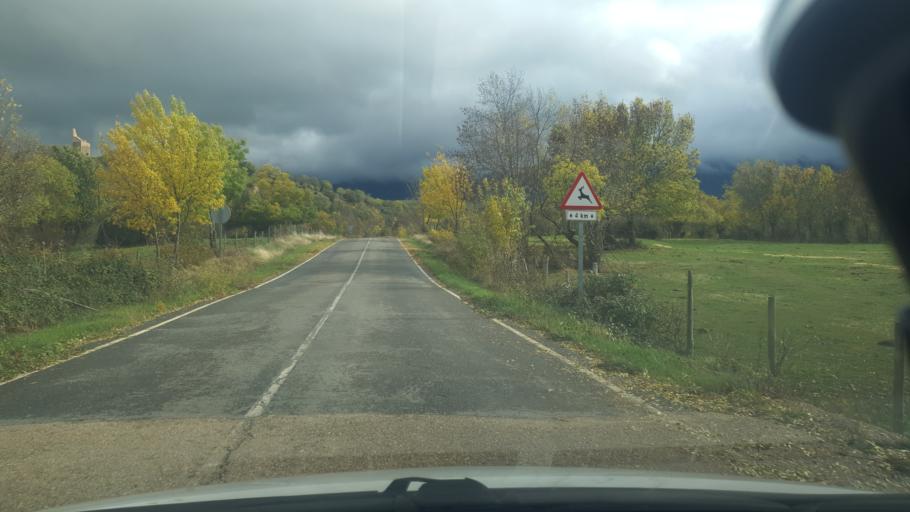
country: ES
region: Castille and Leon
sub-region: Provincia de Segovia
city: Gallegos
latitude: 41.0828
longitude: -3.7943
